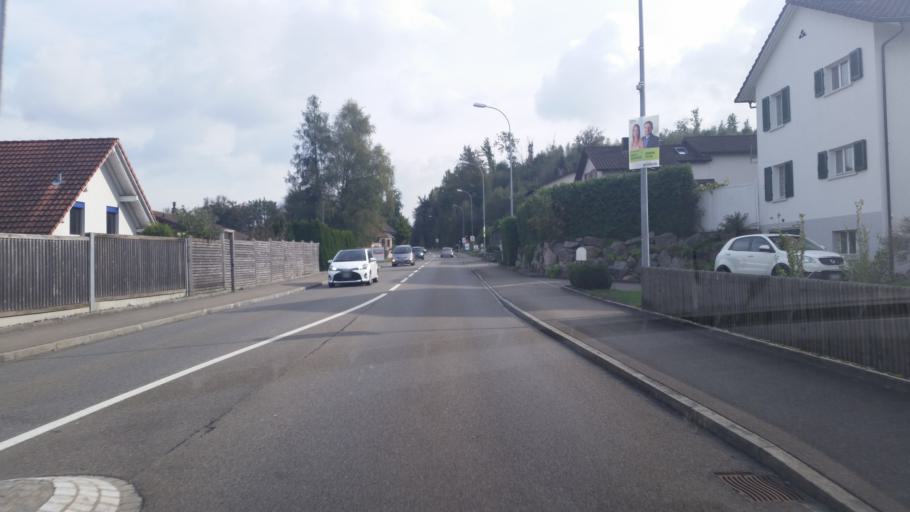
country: CH
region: Aargau
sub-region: Bezirk Baden
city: Kunten
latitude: 47.3663
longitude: 8.3140
